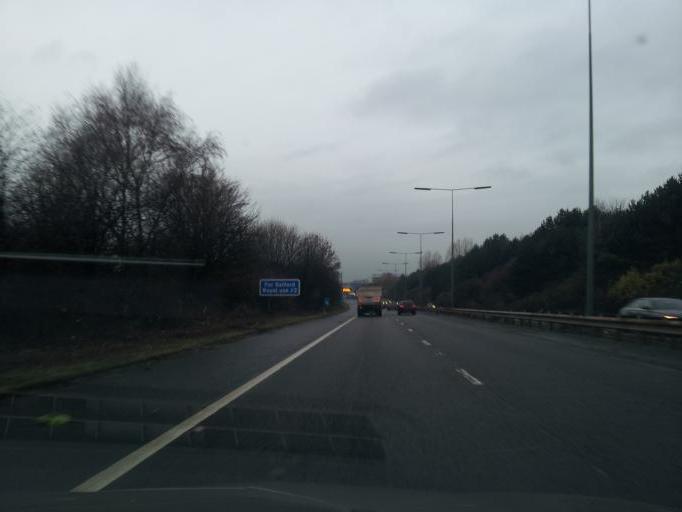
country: GB
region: England
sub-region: Trafford
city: Trafford Park
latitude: 53.4843
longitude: -2.3144
